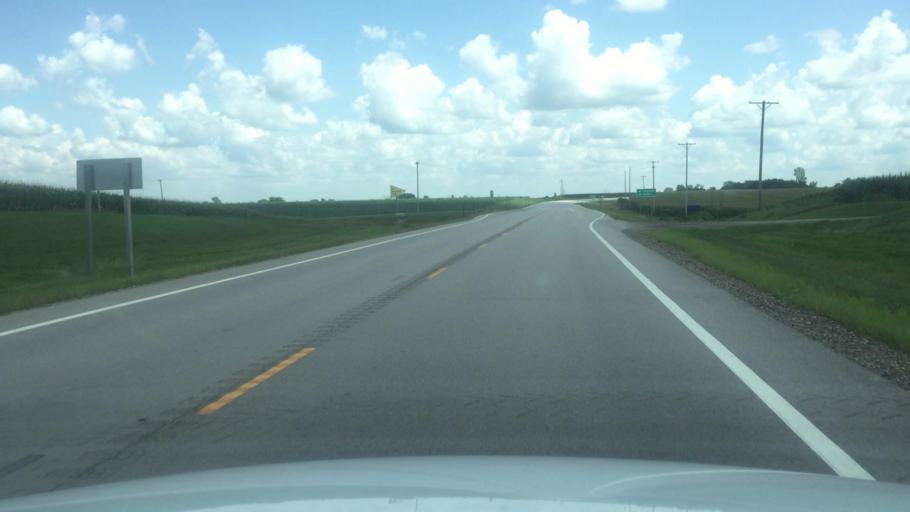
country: US
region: Kansas
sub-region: Brown County
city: Horton
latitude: 39.6673
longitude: -95.4268
